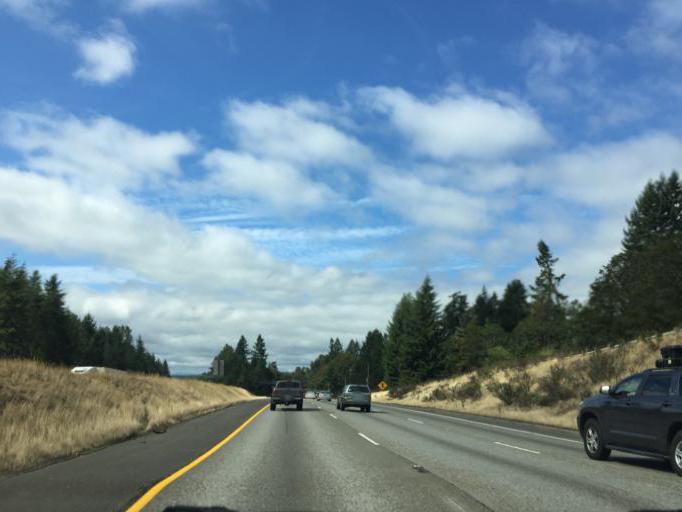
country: US
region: Washington
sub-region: Pierce County
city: DuPont
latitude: 47.0827
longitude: -122.6707
